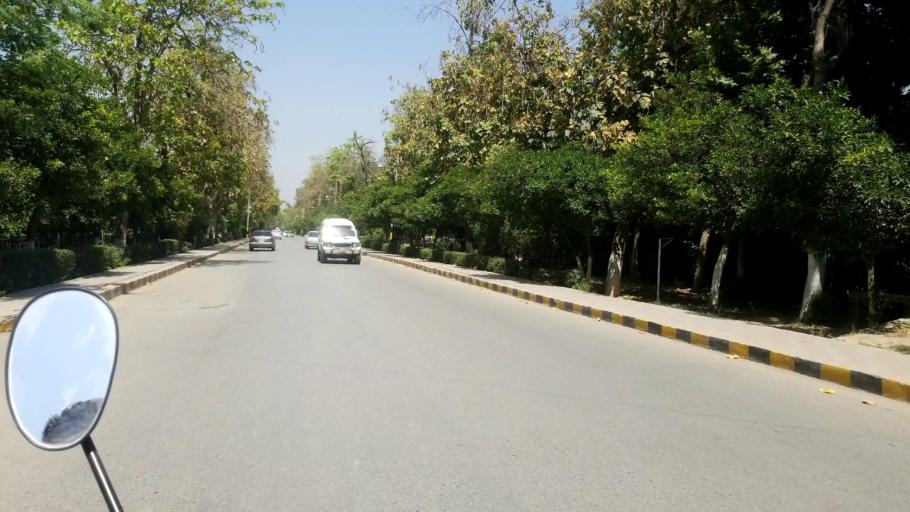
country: PK
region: Khyber Pakhtunkhwa
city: Peshawar
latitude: 34.0019
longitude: 71.4863
